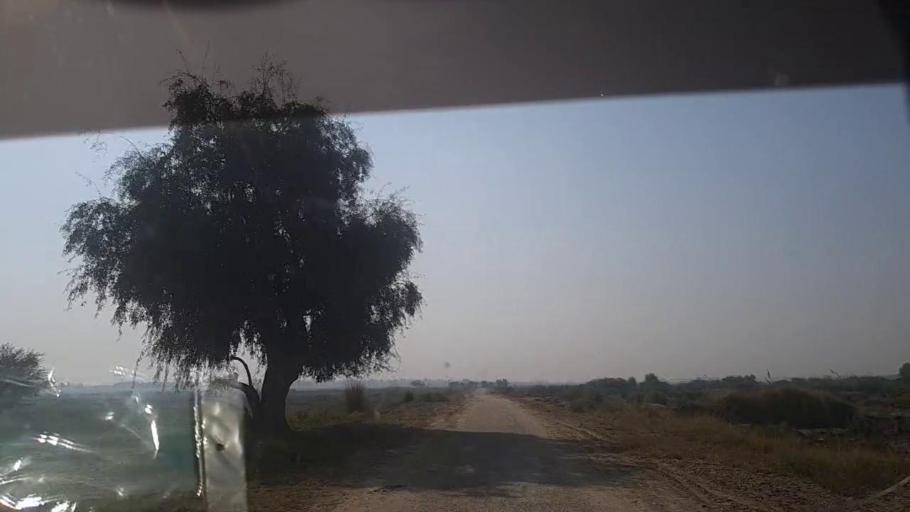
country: PK
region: Sindh
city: Khairpur
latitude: 27.4634
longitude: 68.7394
